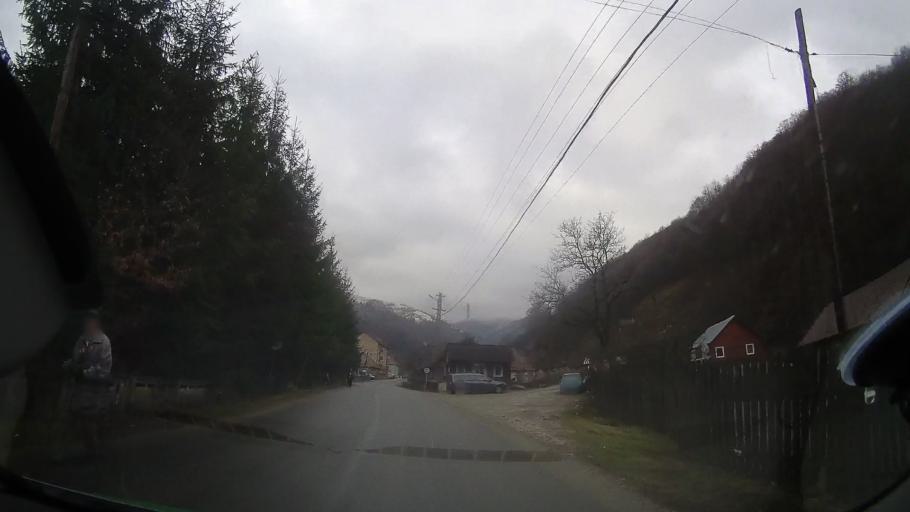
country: RO
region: Cluj
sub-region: Comuna Maguri-Racatau
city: Maguri-Racatau
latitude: 46.6488
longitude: 23.1972
